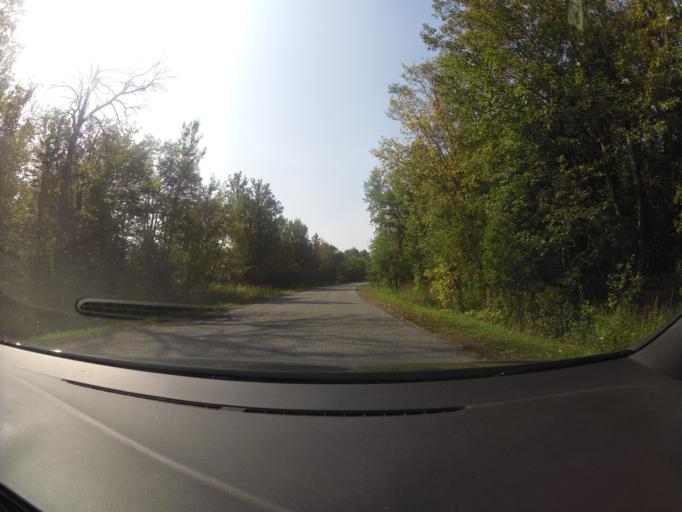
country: CA
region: Ontario
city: Bells Corners
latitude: 45.3784
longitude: -75.9792
